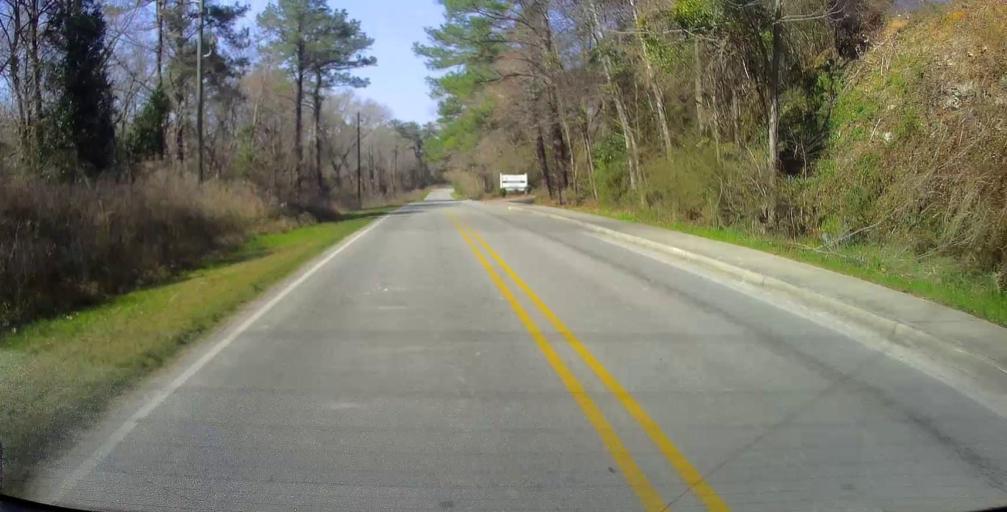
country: US
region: Georgia
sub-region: Bibb County
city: Macon
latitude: 32.8822
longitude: -83.6094
